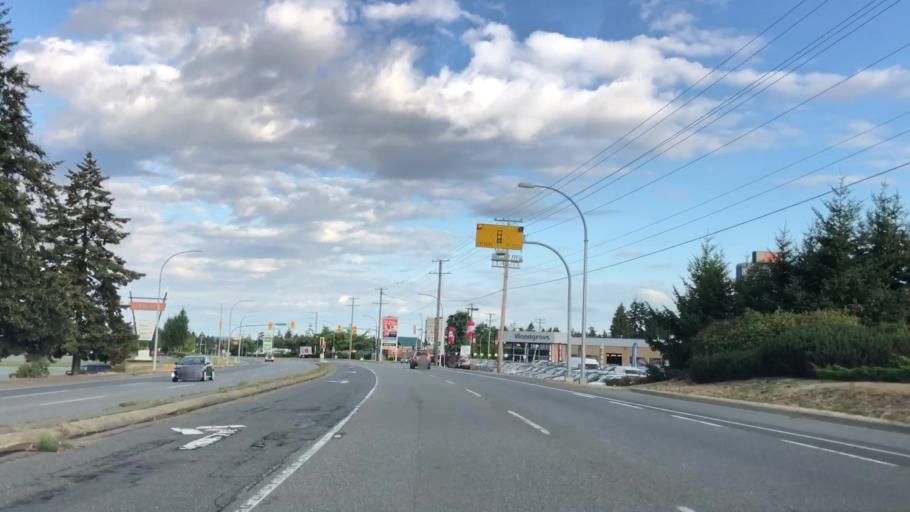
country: CA
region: British Columbia
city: Nanaimo
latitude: 49.2377
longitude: -124.0475
